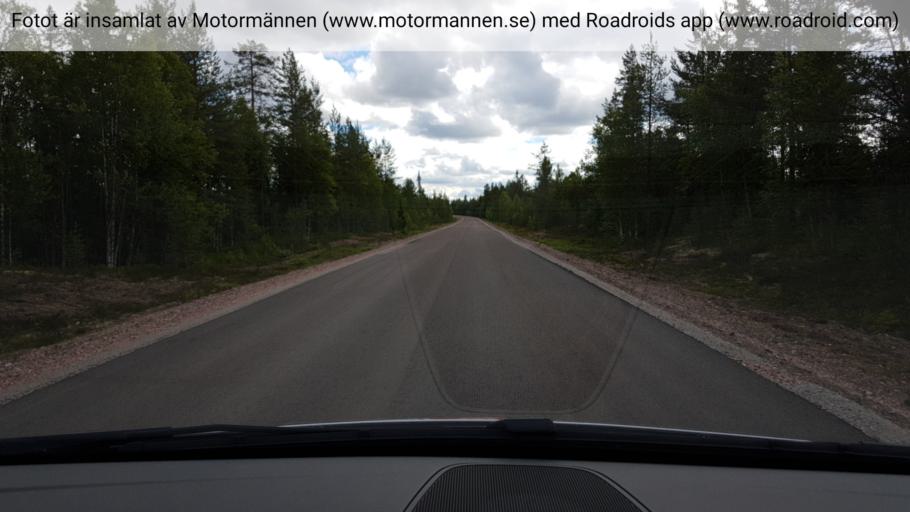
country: SE
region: Jaemtland
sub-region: Harjedalens Kommun
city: Sveg
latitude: 61.6436
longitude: 14.1800
